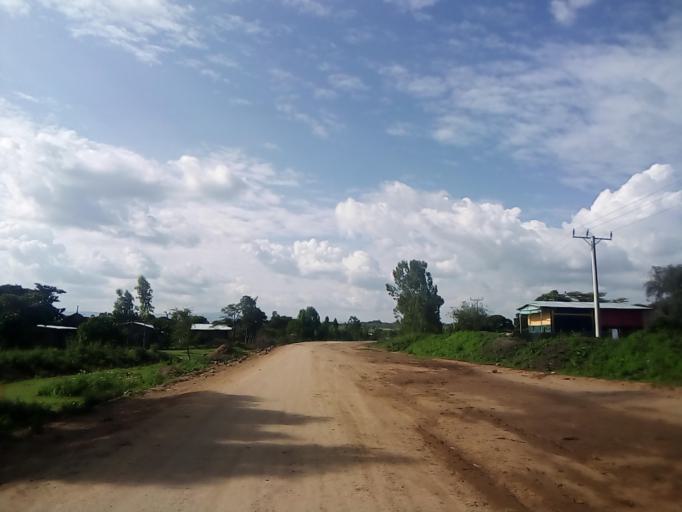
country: ET
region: Southern Nations, Nationalities, and People's Region
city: K'olito
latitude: 7.6160
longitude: 38.0644
